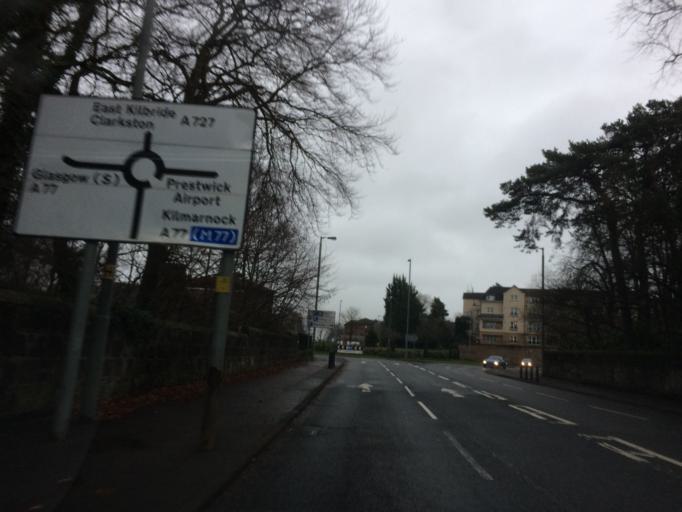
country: GB
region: Scotland
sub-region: East Renfrewshire
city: Giffnock
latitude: 55.7966
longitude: -4.3034
